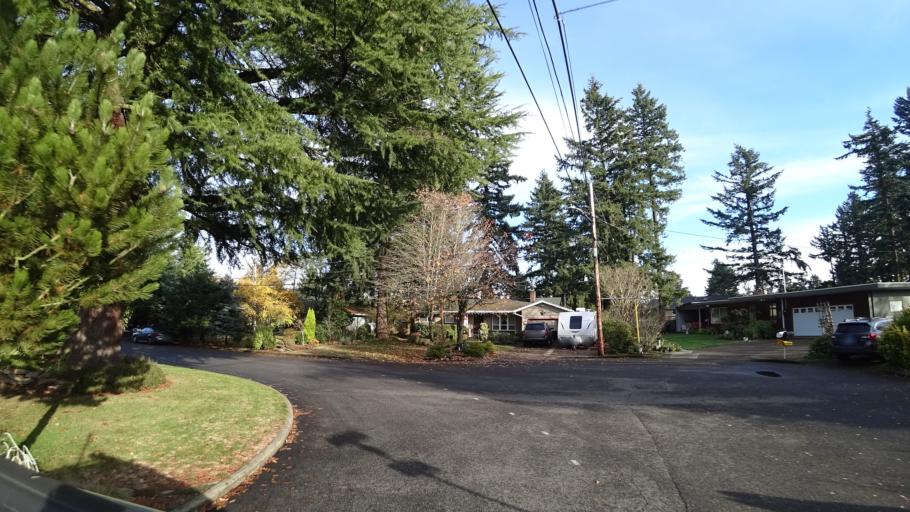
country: US
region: Oregon
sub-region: Multnomah County
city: Lents
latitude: 45.5218
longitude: -122.5281
